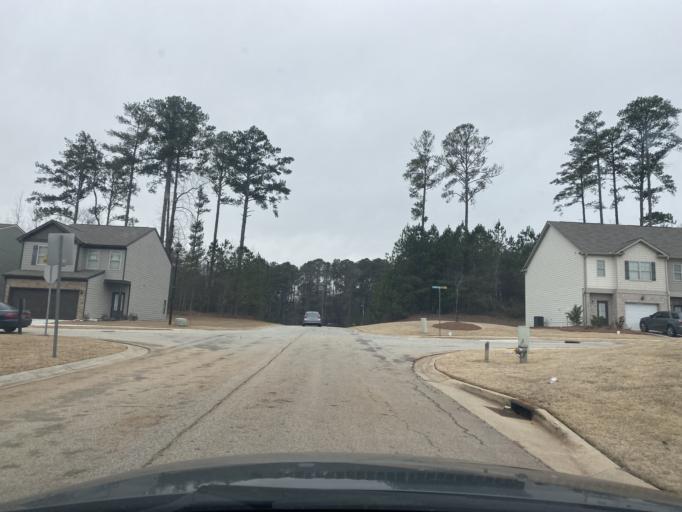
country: US
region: Georgia
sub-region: DeKalb County
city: Pine Mountain
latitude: 33.6893
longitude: -84.1542
